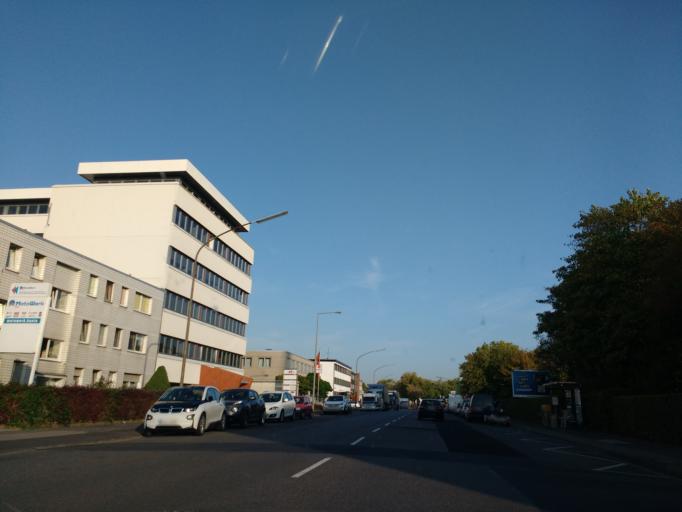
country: DE
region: North Rhine-Westphalia
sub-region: Regierungsbezirk Koln
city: Bilderstoeckchen
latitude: 50.9804
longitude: 6.9188
